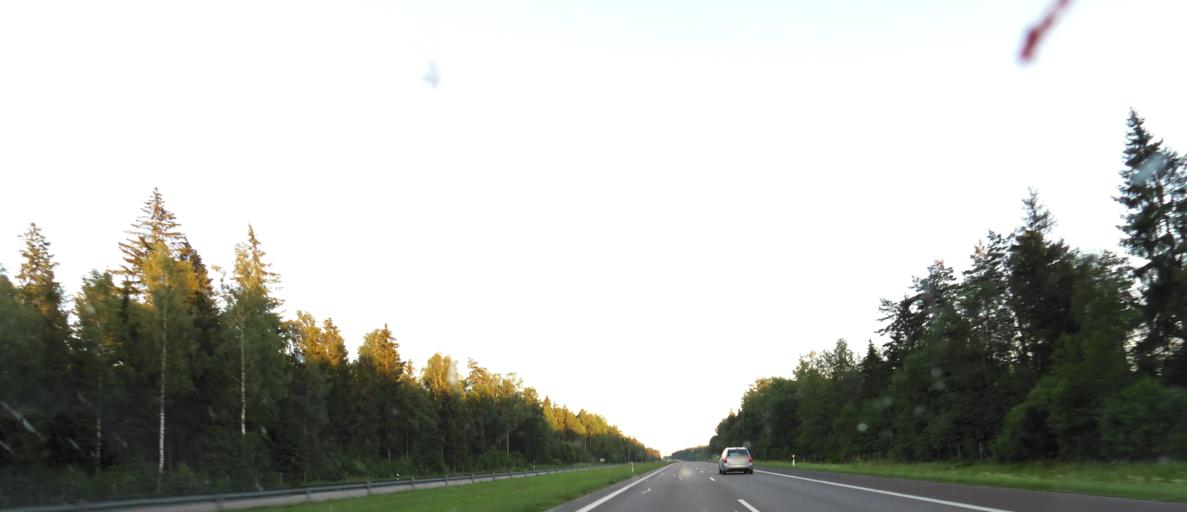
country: LT
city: Sirvintos
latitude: 54.9667
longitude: 24.9505
